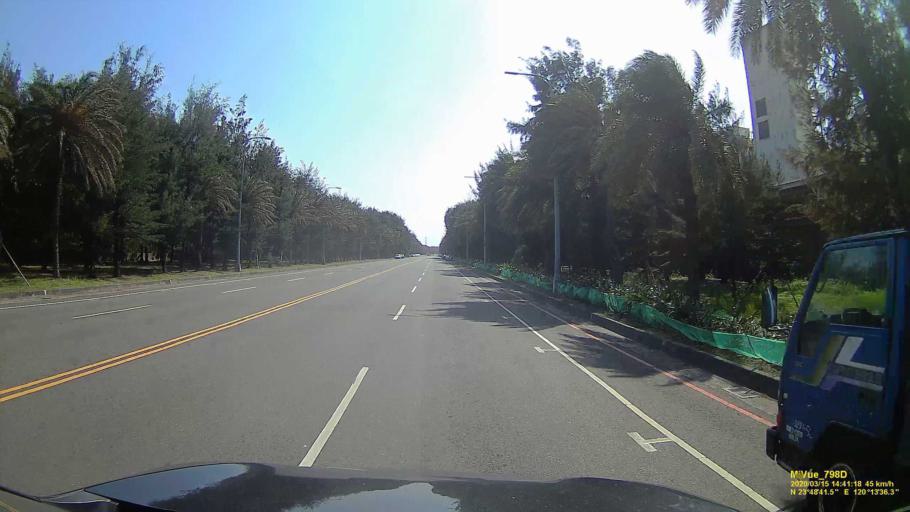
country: TW
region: Taiwan
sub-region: Yunlin
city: Douliu
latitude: 23.8114
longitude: 120.2266
